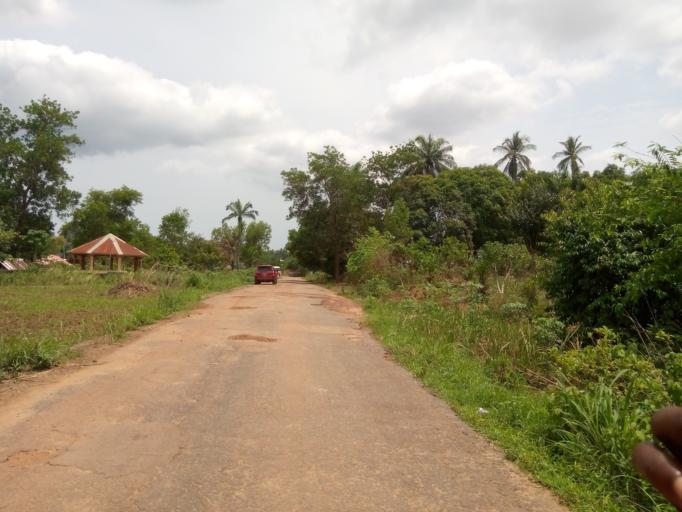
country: SL
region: Western Area
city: Waterloo
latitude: 8.3494
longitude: -12.9826
